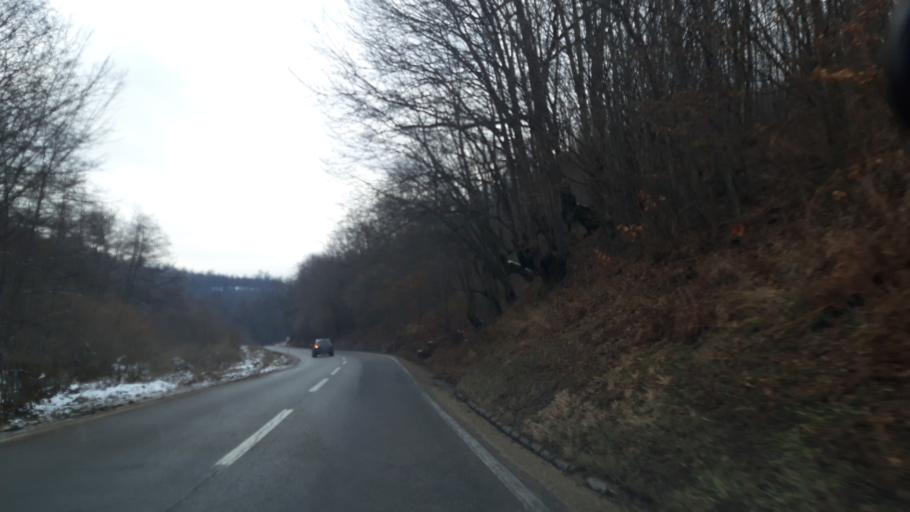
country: BA
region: Republika Srpska
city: Vlasenica
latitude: 44.1757
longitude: 19.0121
